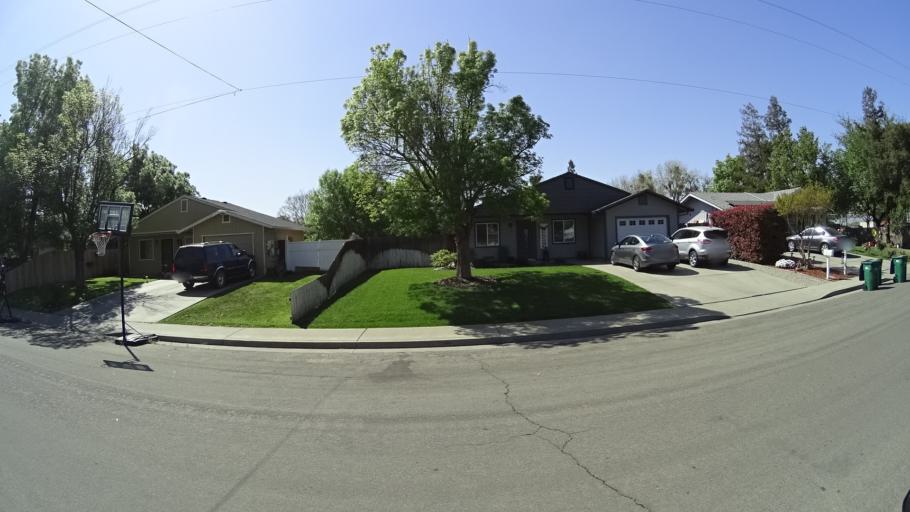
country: US
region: California
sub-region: Glenn County
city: Willows
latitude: 39.5128
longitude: -122.1963
